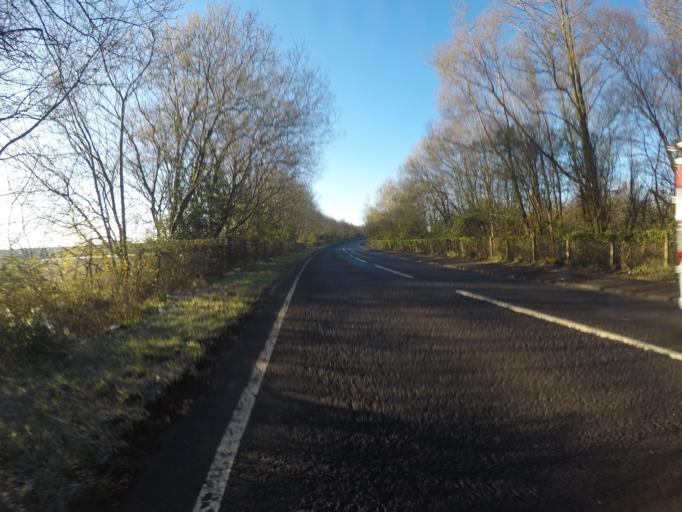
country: GB
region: Scotland
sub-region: North Ayrshire
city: Stevenston
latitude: 55.6398
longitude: -4.7406
